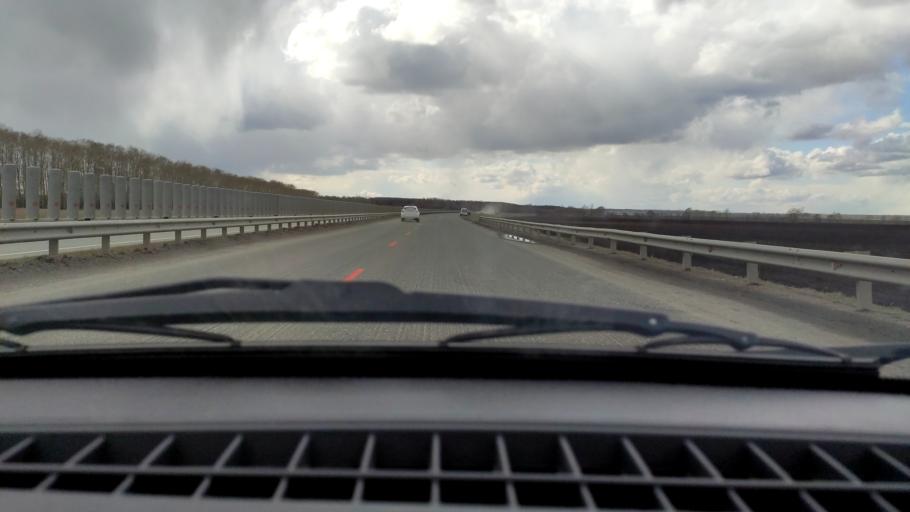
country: RU
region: Bashkortostan
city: Kushnarenkovo
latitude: 55.0611
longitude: 55.3914
